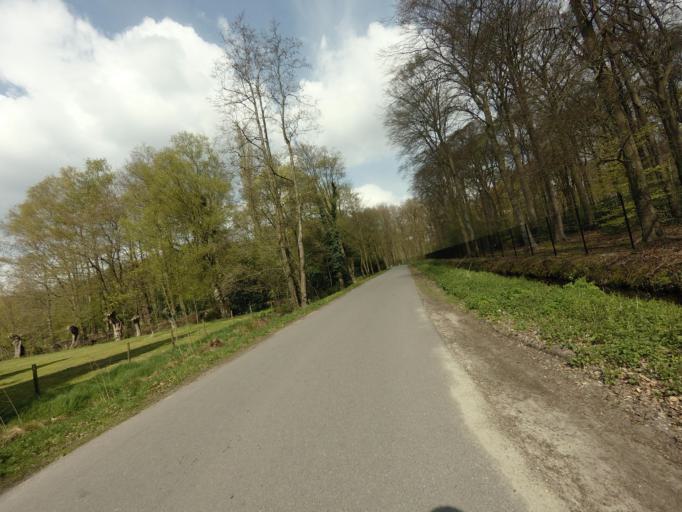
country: NL
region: Utrecht
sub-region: Gemeente Utrechtse Heuvelrug
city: Doorn
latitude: 52.0292
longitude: 5.3348
